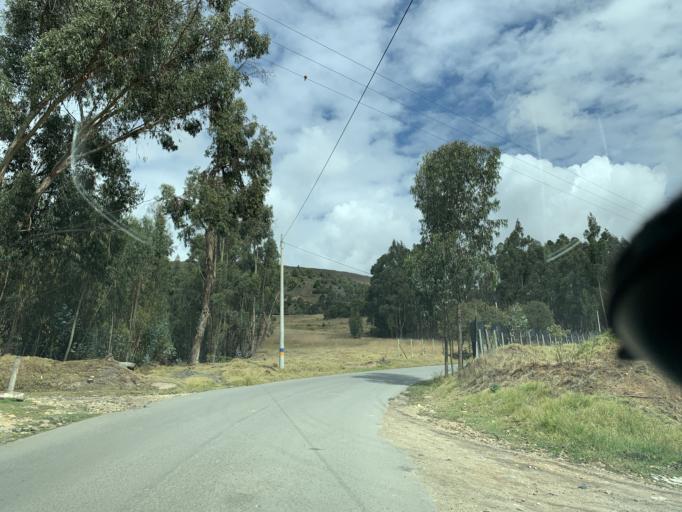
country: CO
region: Boyaca
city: Siachoque
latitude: 5.5683
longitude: -73.2662
